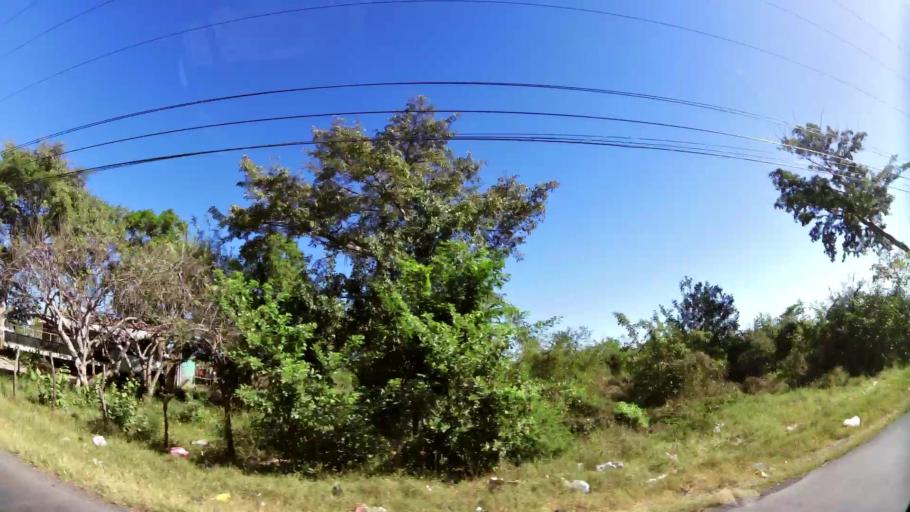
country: SV
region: San Miguel
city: San Miguel
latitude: 13.4634
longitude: -88.1525
